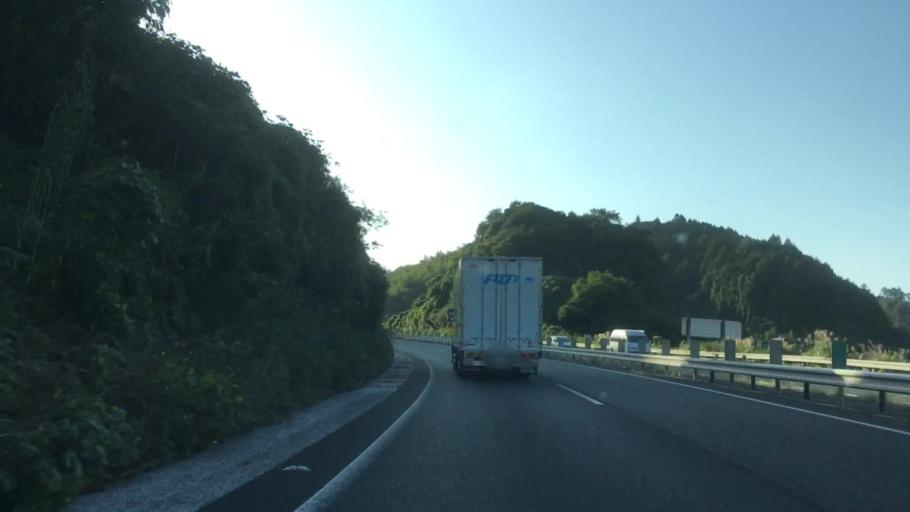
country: JP
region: Yamaguchi
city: Onoda
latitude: 34.1164
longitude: 131.1262
